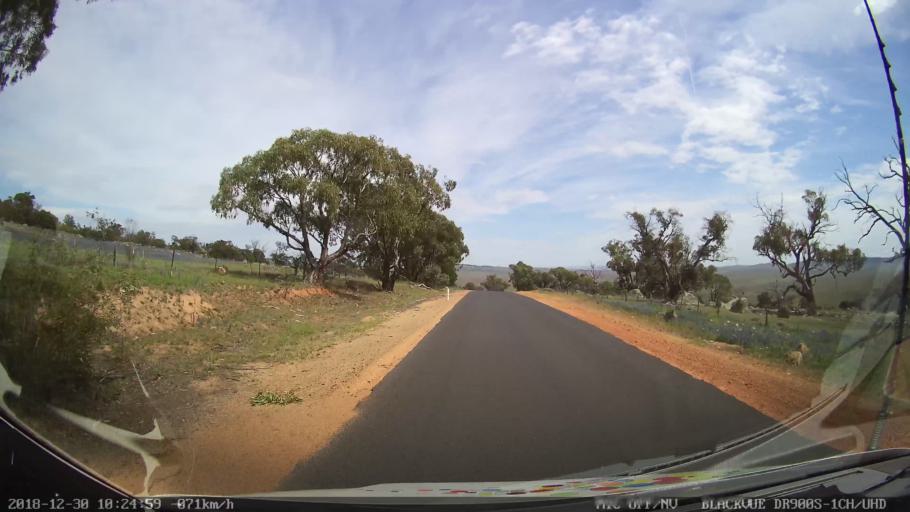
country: AU
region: New South Wales
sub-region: Snowy River
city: Berridale
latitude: -36.5298
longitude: 148.9625
